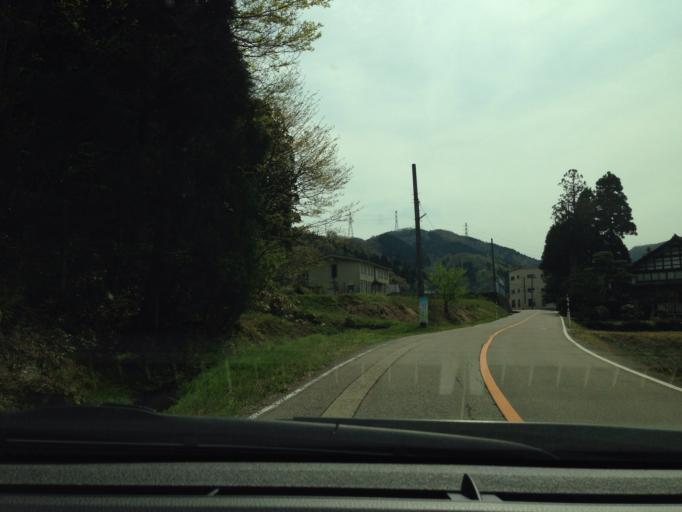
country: JP
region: Toyama
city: Fukumitsu
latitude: 36.5001
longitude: 136.8444
